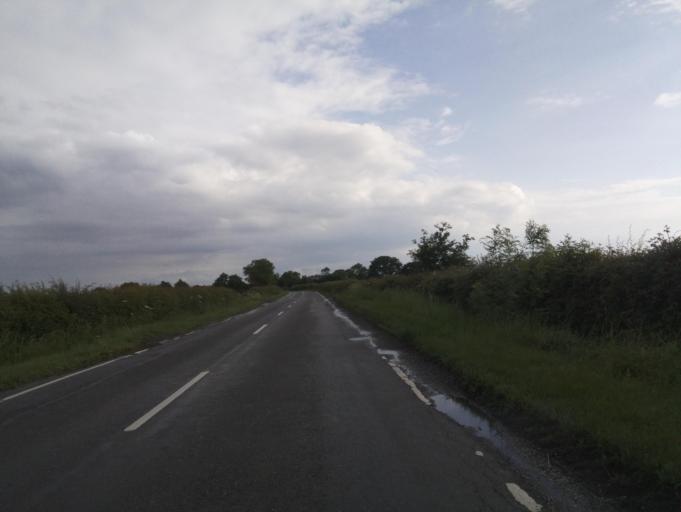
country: GB
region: England
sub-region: Lincolnshire
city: Great Gonerby
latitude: 53.0139
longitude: -0.6618
